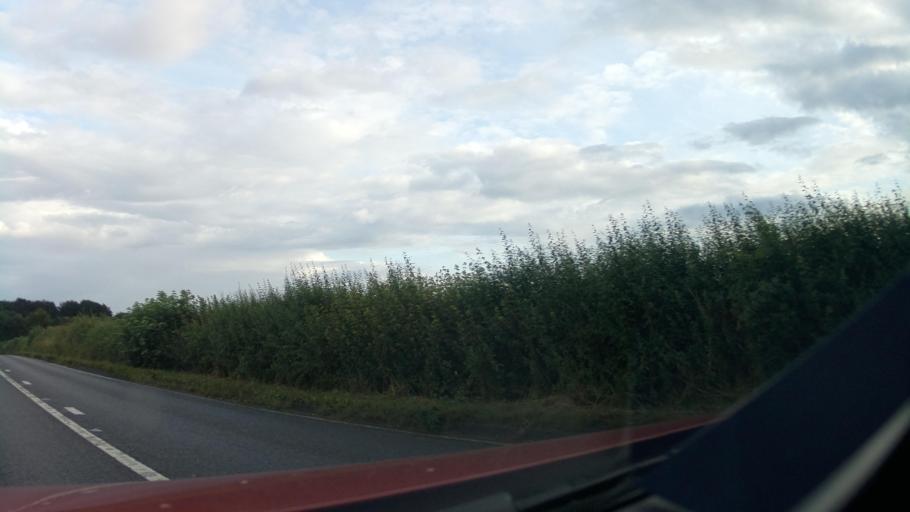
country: GB
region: England
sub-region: Oxfordshire
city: Kidlington
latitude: 51.8487
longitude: -1.3130
